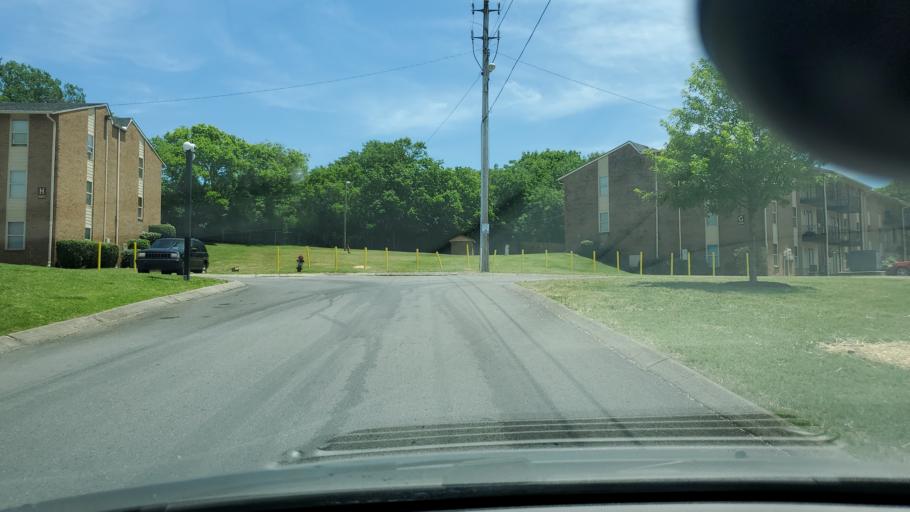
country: US
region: Tennessee
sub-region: Davidson County
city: Nashville
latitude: 36.2125
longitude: -86.7599
